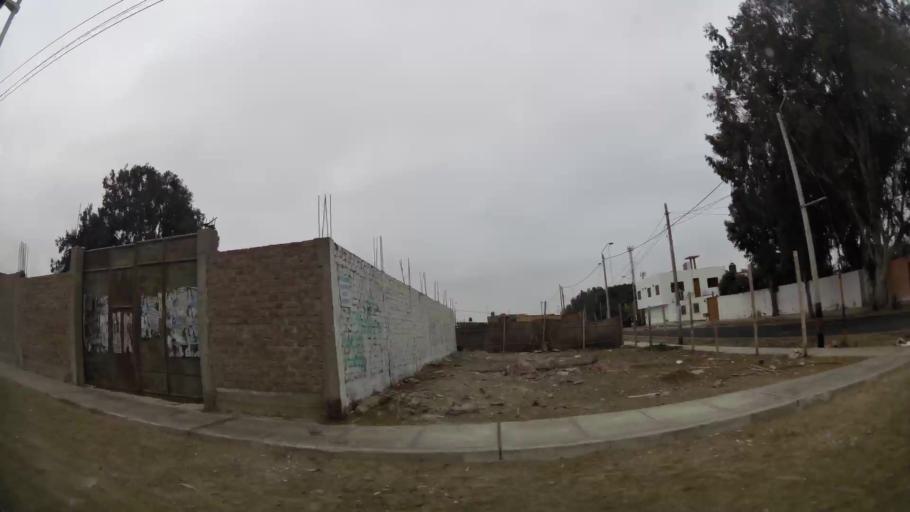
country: PE
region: Ica
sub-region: Provincia de Pisco
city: Paracas
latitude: -13.8370
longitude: -76.2498
